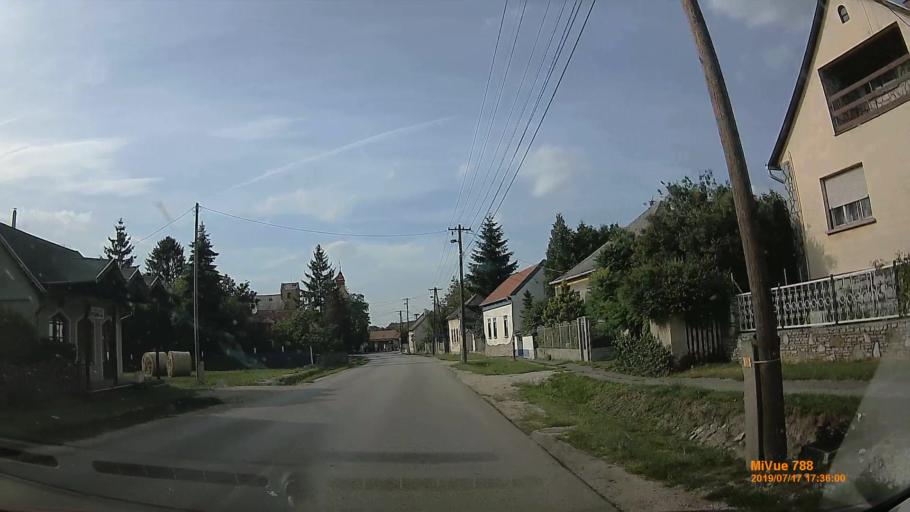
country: HU
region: Veszprem
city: Ajka
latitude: 47.0691
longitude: 17.5511
